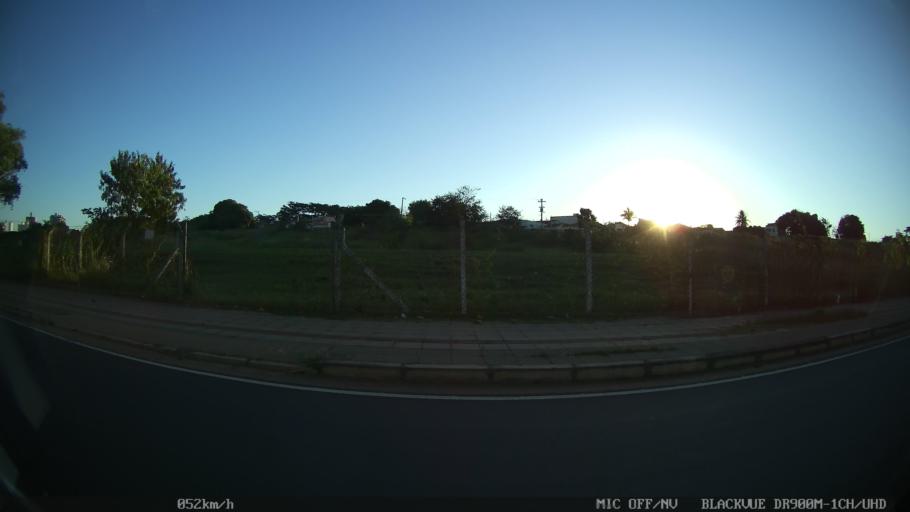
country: BR
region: Sao Paulo
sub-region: Sao Jose Do Rio Preto
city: Sao Jose do Rio Preto
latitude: -20.7953
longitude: -49.3770
